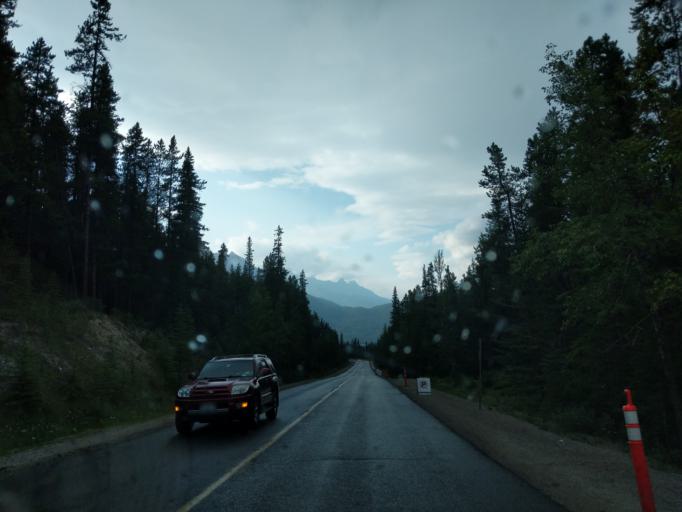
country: CA
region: Alberta
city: Banff
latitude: 51.1566
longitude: -115.5640
